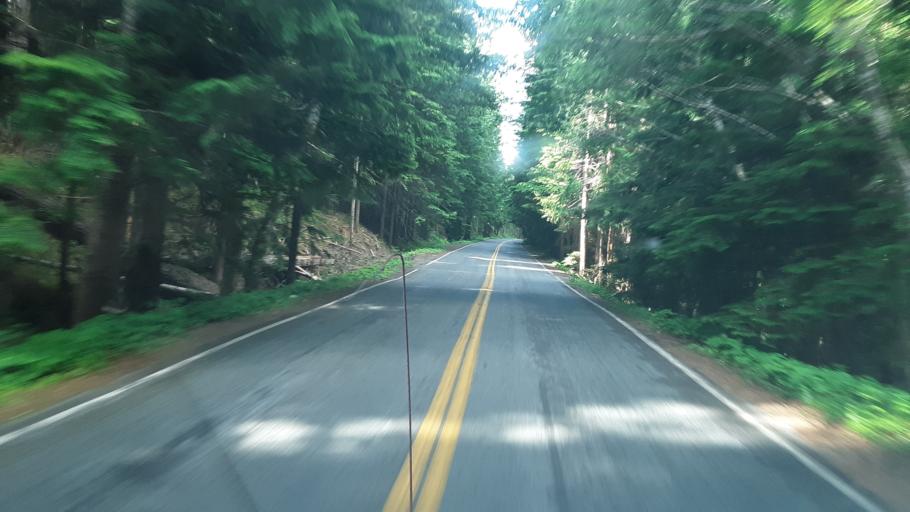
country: US
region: Washington
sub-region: Pierce County
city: Buckley
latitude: 46.7605
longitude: -121.5521
